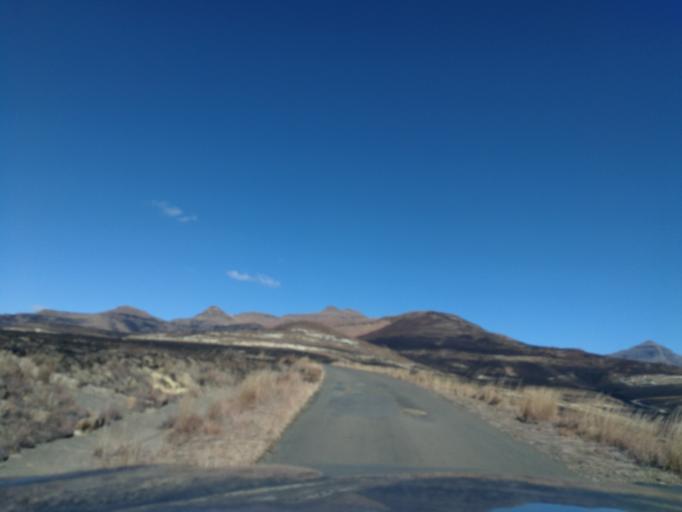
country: ZA
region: Orange Free State
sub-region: Thabo Mofutsanyana District Municipality
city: Phuthaditjhaba
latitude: -28.5154
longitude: 28.6221
